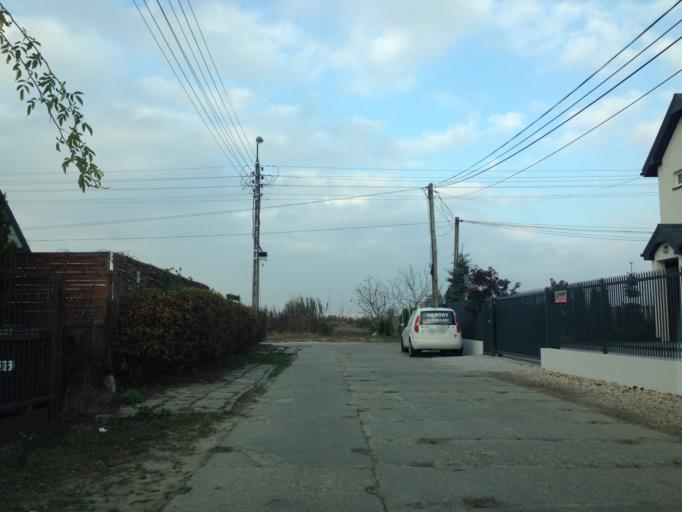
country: PL
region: Masovian Voivodeship
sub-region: Powiat pruszkowski
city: Rybie
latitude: 52.1621
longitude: 20.9358
